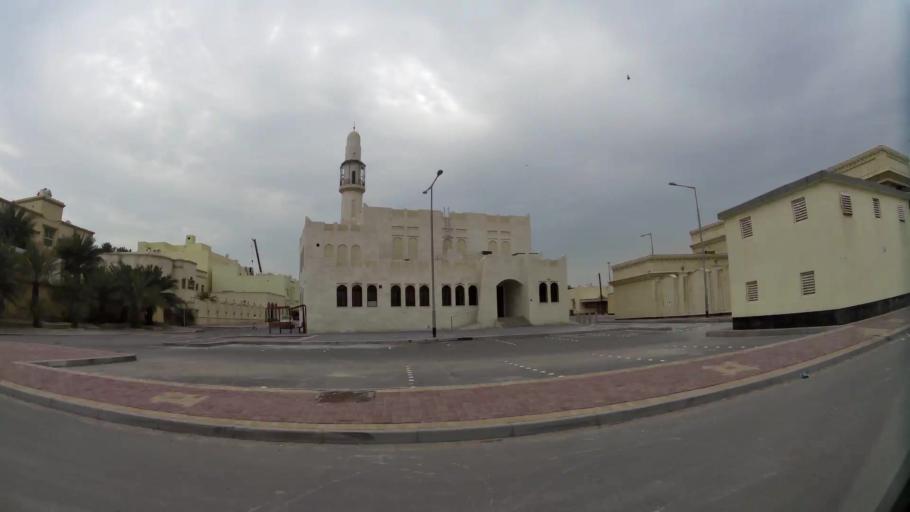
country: BH
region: Northern
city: Ar Rifa'
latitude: 26.0584
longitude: 50.6187
